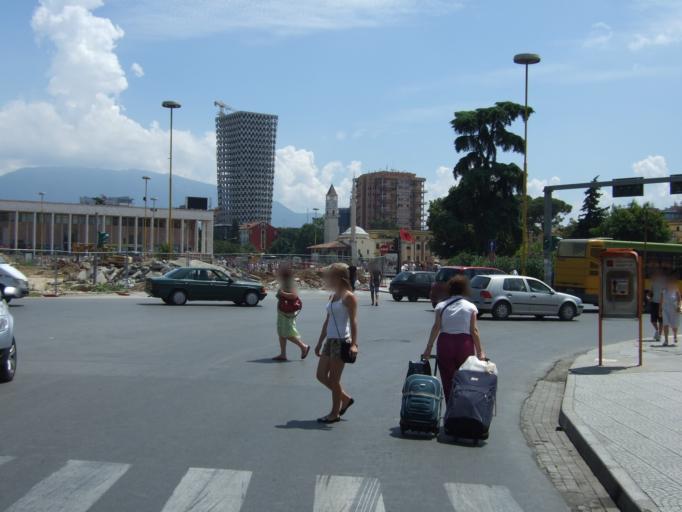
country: AL
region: Tirane
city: Tirana
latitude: 41.3291
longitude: 19.8157
